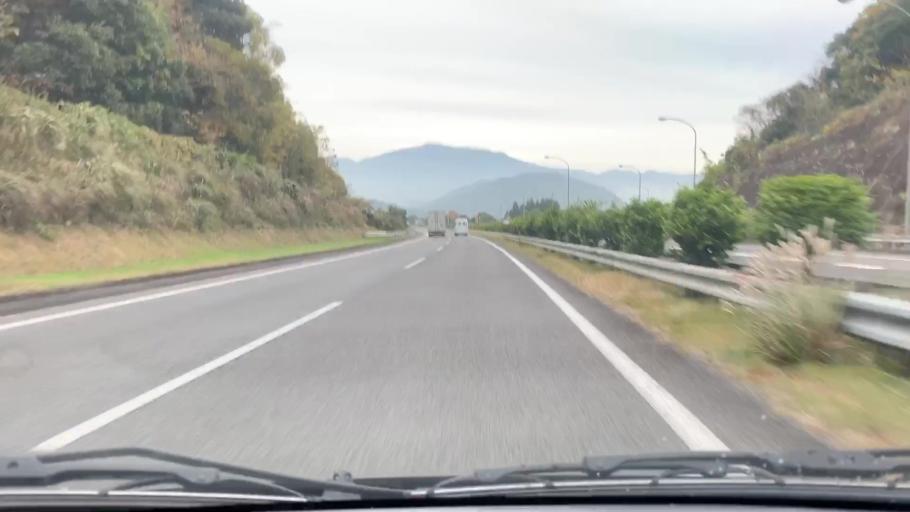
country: JP
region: Saga Prefecture
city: Takeocho-takeo
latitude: 33.2512
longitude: 130.0769
